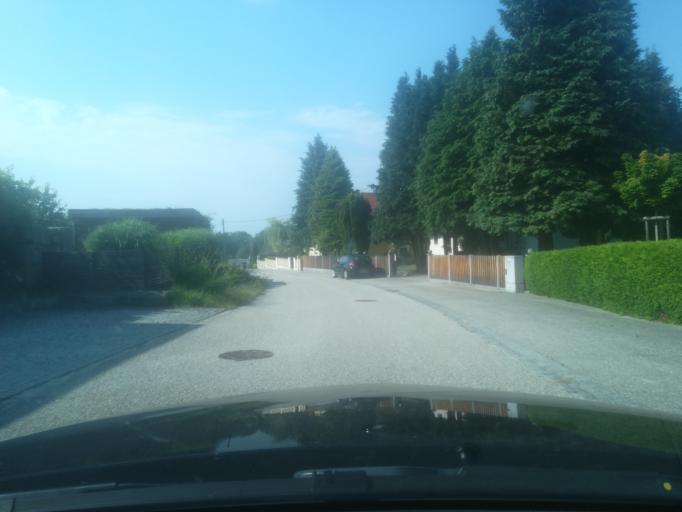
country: AT
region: Upper Austria
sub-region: Wels-Land
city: Holzhausen
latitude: 48.2322
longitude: 14.0779
